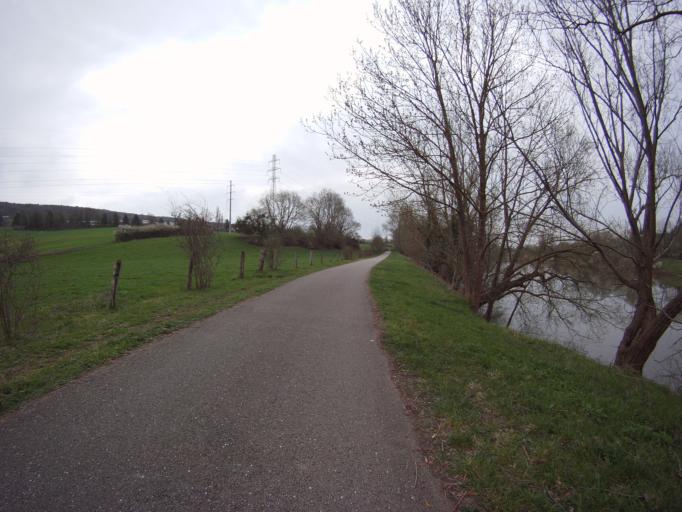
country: FR
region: Lorraine
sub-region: Departement de Meurthe-et-Moselle
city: Champigneulles
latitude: 48.7308
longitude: 6.1752
